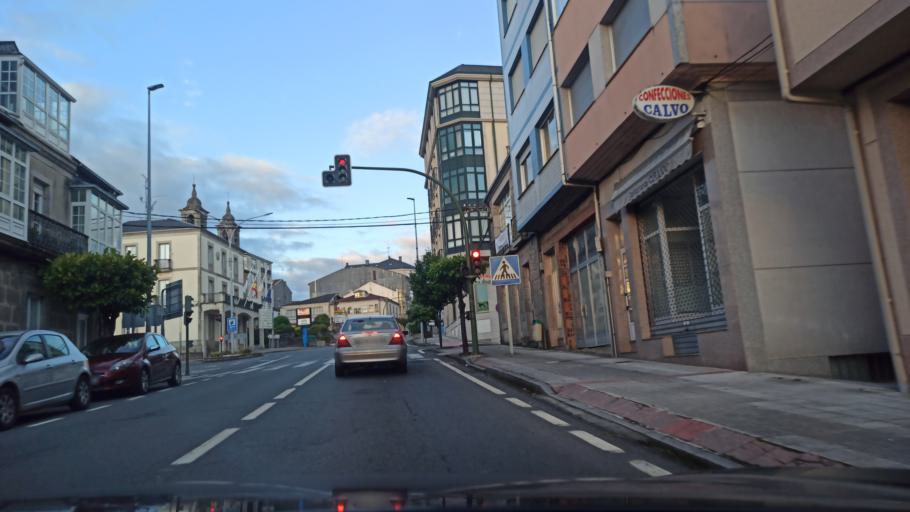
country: ES
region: Galicia
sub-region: Provincia de Lugo
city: Monterroso
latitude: 42.7930
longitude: -7.8374
